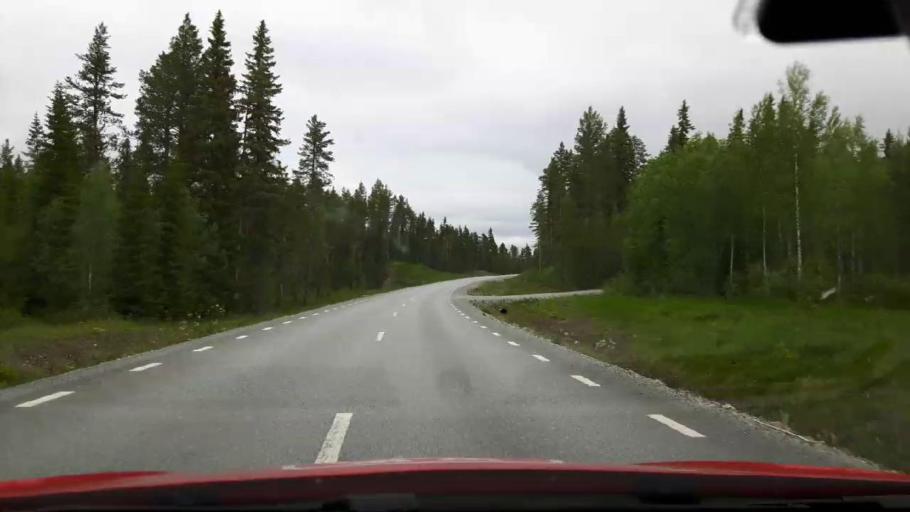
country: SE
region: Jaemtland
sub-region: OEstersunds Kommun
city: Lit
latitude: 63.7101
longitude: 14.6955
